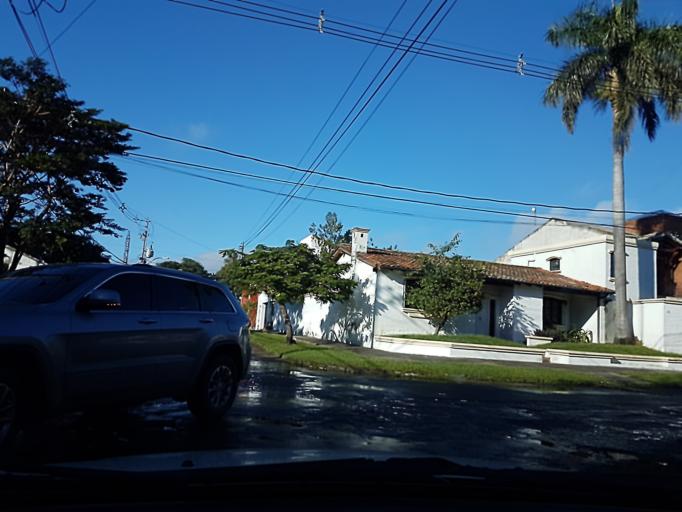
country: PY
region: Asuncion
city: Asuncion
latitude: -25.2859
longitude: -57.5929
